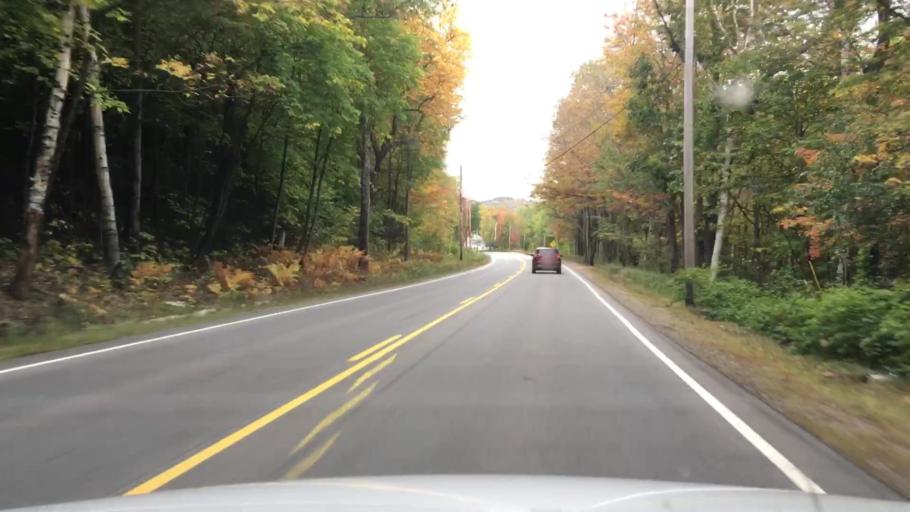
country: US
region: New Hampshire
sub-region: Coos County
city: Gorham
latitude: 44.4068
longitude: -71.0960
